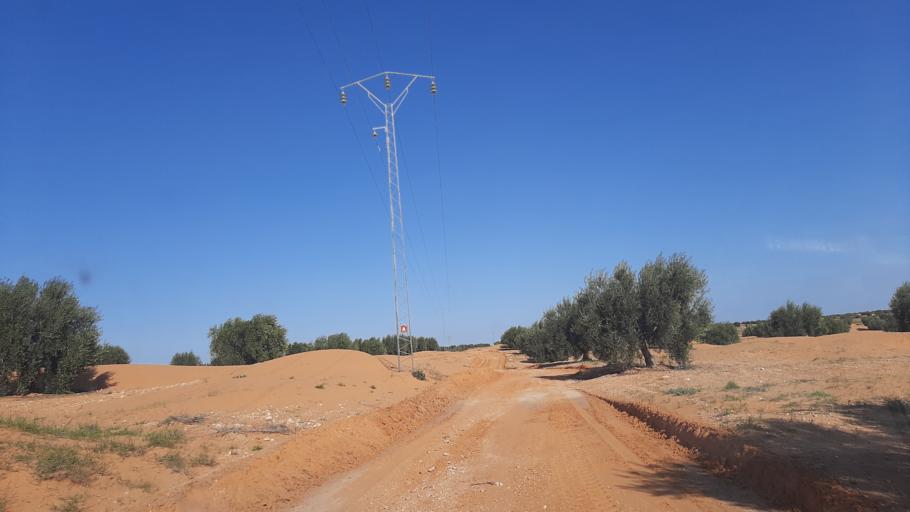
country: TN
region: Madanin
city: Medenine
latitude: 33.2827
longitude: 10.7834
